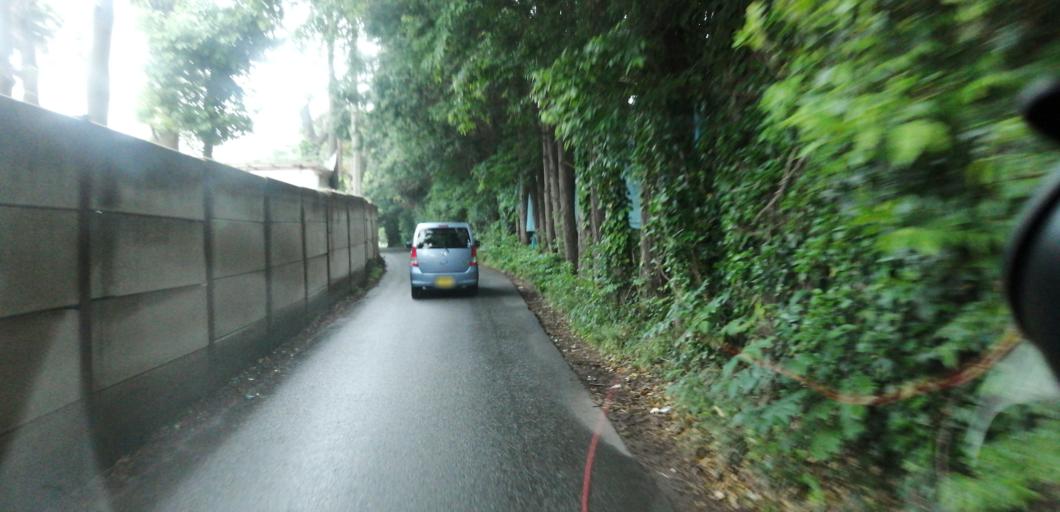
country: JP
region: Chiba
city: Ichihara
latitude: 35.4816
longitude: 140.1474
